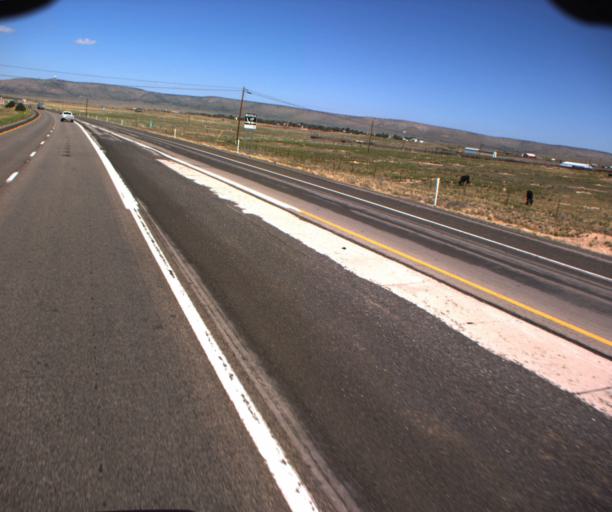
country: US
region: Arizona
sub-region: Yavapai County
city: Paulden
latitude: 35.3124
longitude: -112.8593
